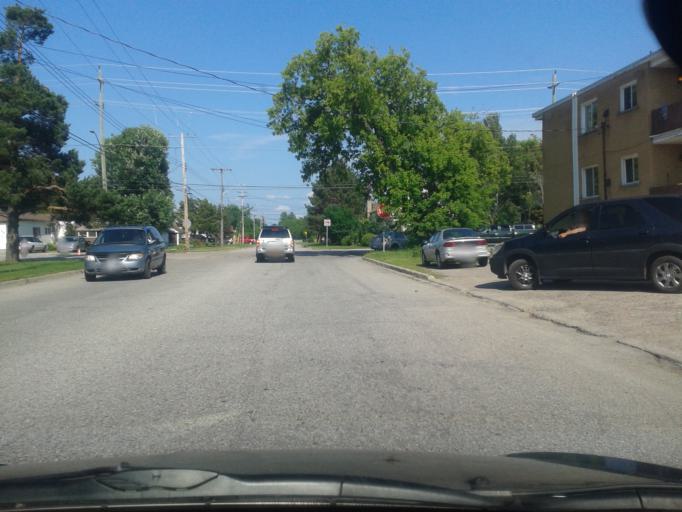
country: CA
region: Ontario
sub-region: Nipissing District
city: North Bay
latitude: 46.3256
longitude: -79.4579
